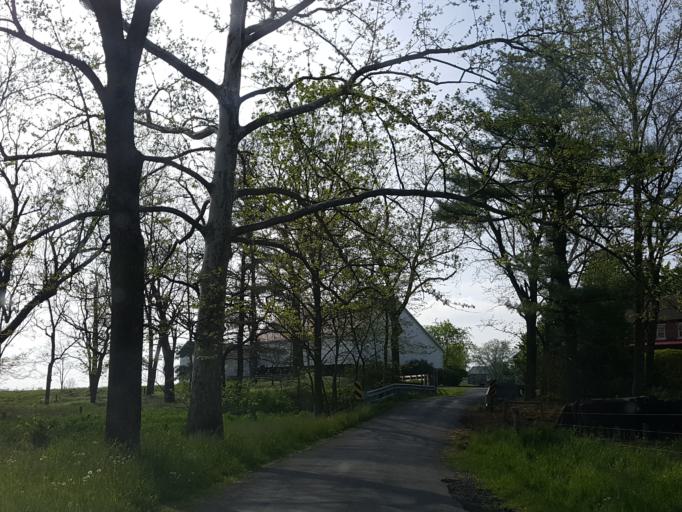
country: US
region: Pennsylvania
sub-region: Lancaster County
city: Elizabethtown
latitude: 40.1957
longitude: -76.5689
